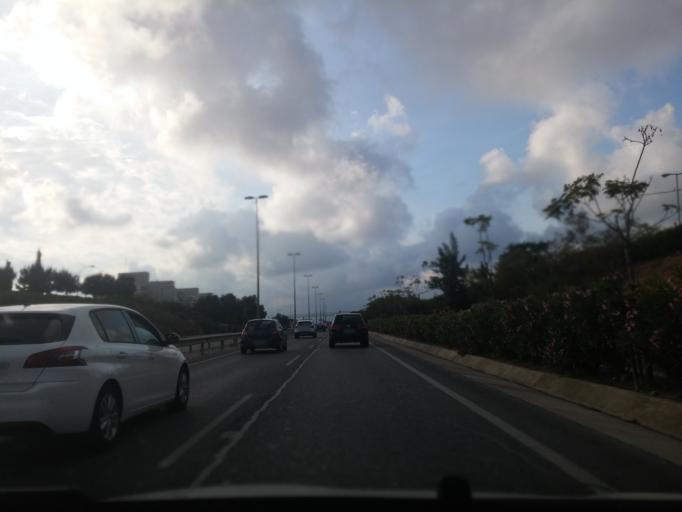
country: ES
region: Valencia
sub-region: Provincia de Alicante
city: Alicante
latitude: 38.3675
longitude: -0.5017
